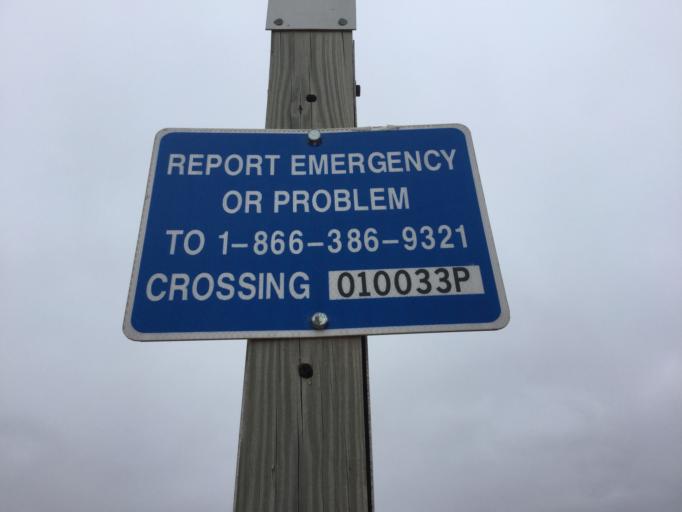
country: US
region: Kansas
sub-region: Pawnee County
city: Larned
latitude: 38.2234
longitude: -99.0408
